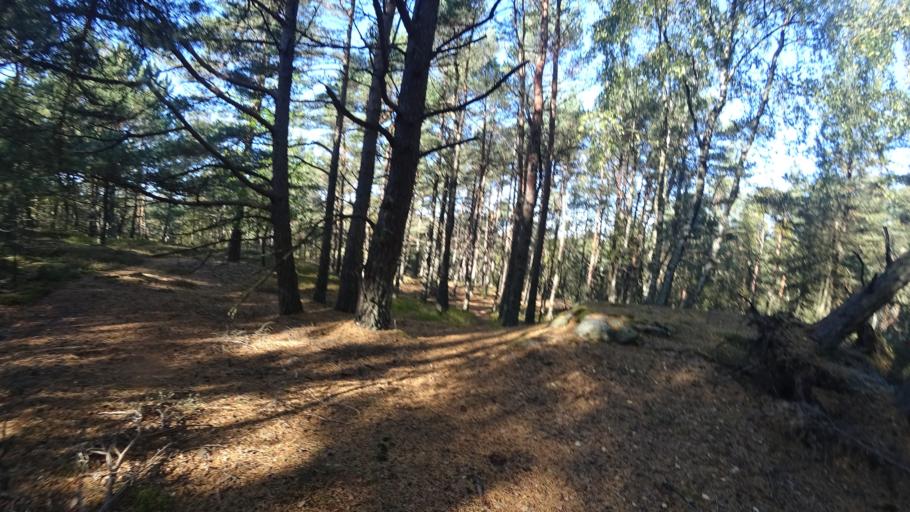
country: SE
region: Vaestra Goetaland
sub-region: Goteborg
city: Goeteborg
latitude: 57.6673
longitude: 11.9604
